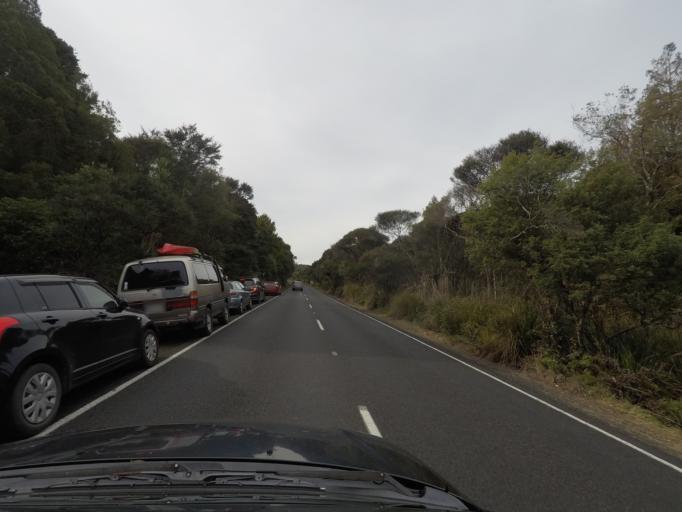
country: NZ
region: Auckland
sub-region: Auckland
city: Titirangi
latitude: -36.9361
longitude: 174.5592
